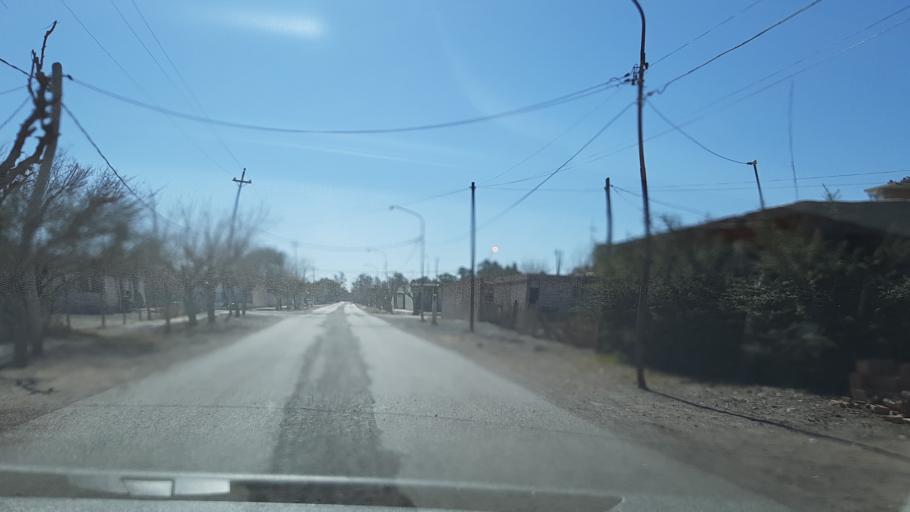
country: AR
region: San Juan
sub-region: Departamento de Zonda
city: Zonda
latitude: -31.5503
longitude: -68.7284
